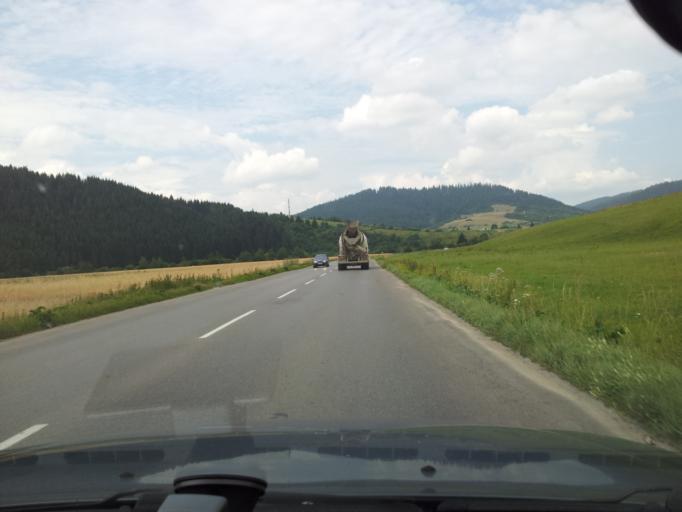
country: SK
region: Zilinsky
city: Namestovo
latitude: 49.3756
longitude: 19.3896
